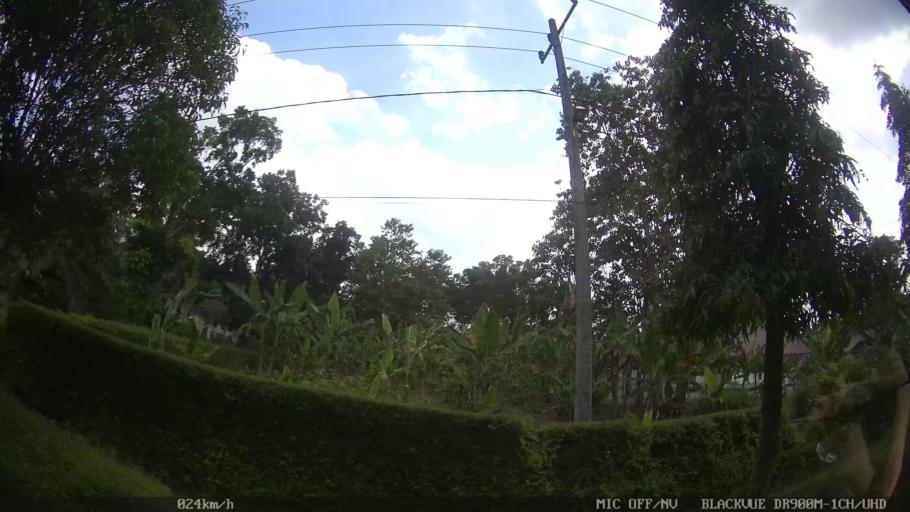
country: ID
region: North Sumatra
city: Binjai
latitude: 3.6354
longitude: 98.5144
